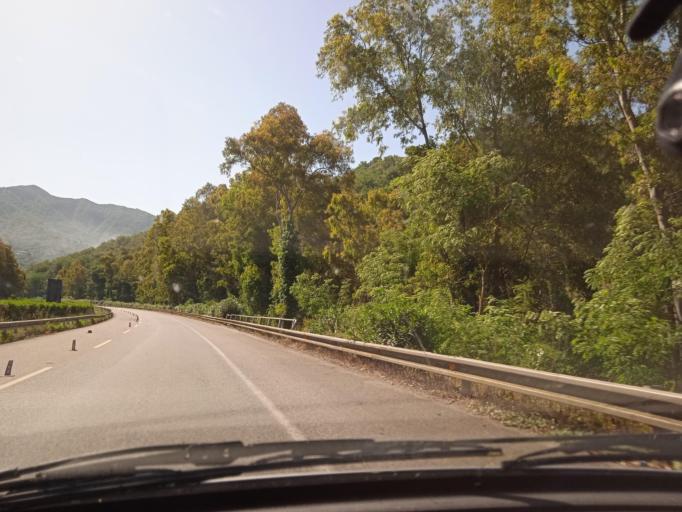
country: IT
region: Sicily
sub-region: Messina
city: Piraino
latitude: 38.1418
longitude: 14.8647
